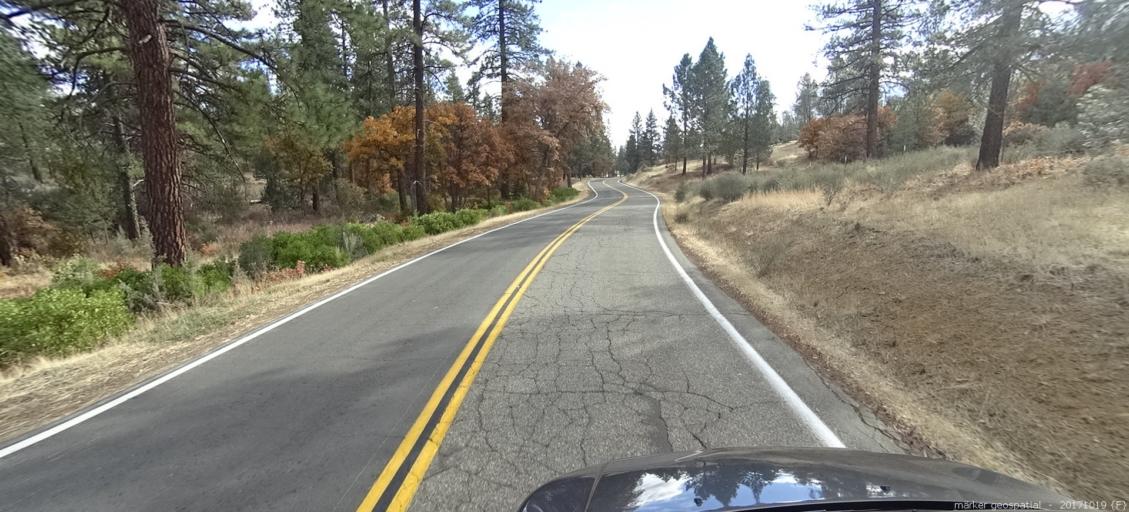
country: US
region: California
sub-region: Shasta County
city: Burney
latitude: 40.9503
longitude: -121.4409
